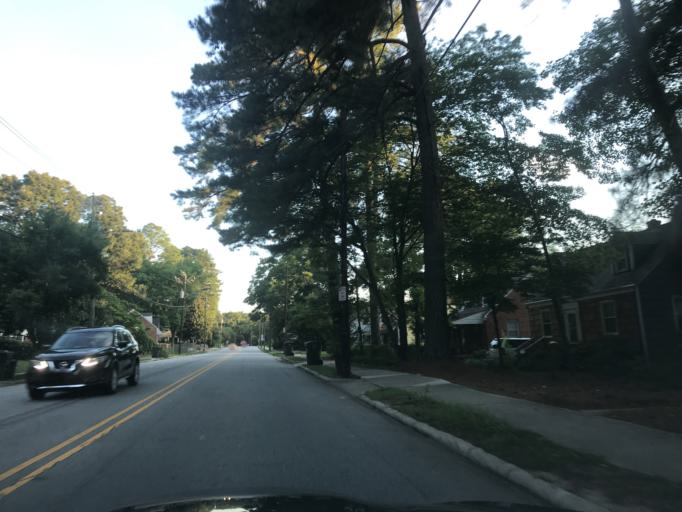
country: US
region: North Carolina
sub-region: Wake County
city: Raleigh
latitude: 35.7953
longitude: -78.6245
